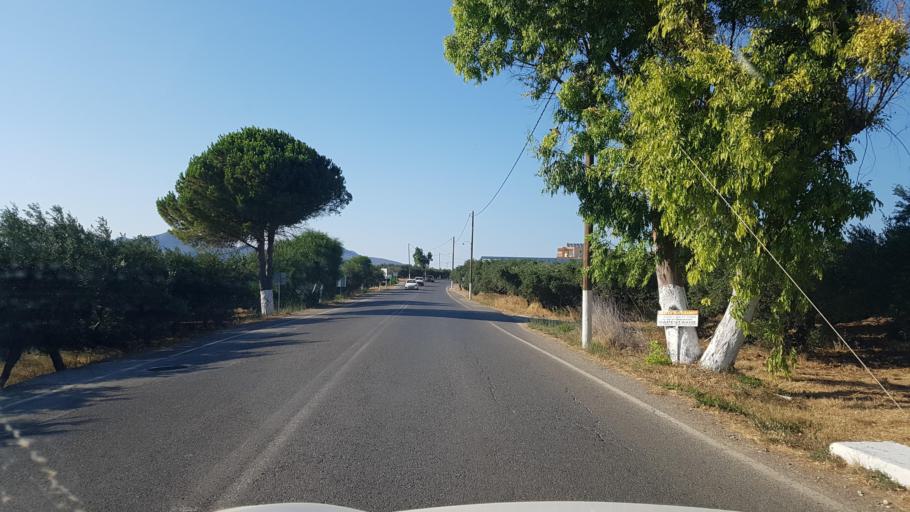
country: GR
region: Crete
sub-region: Nomos Chanias
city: Platanos
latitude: 35.4780
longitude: 23.6045
